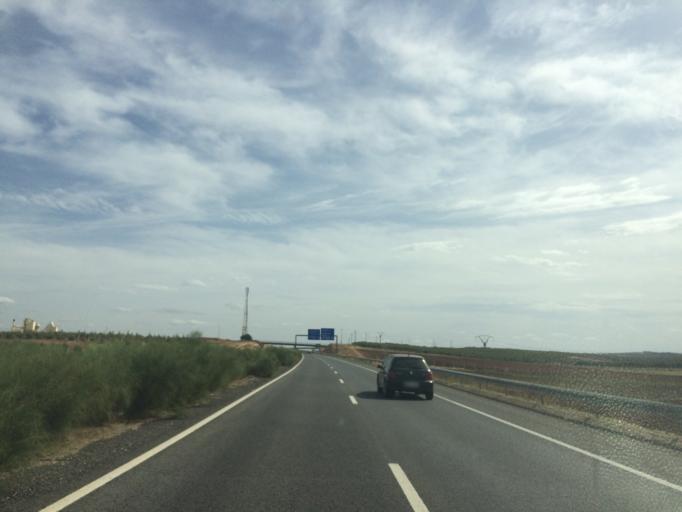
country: MA
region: Meknes-Tafilalet
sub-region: Meknes
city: Meknes
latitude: 33.8465
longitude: -5.6141
